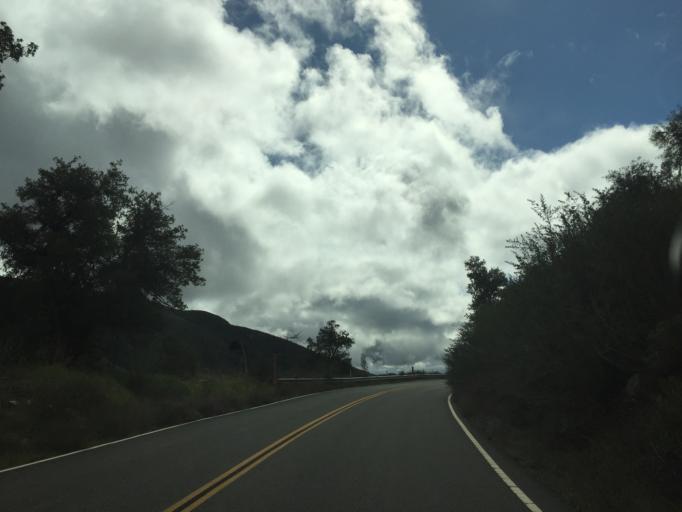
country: US
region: California
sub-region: Los Angeles County
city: Glendora
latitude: 34.2893
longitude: -117.8408
